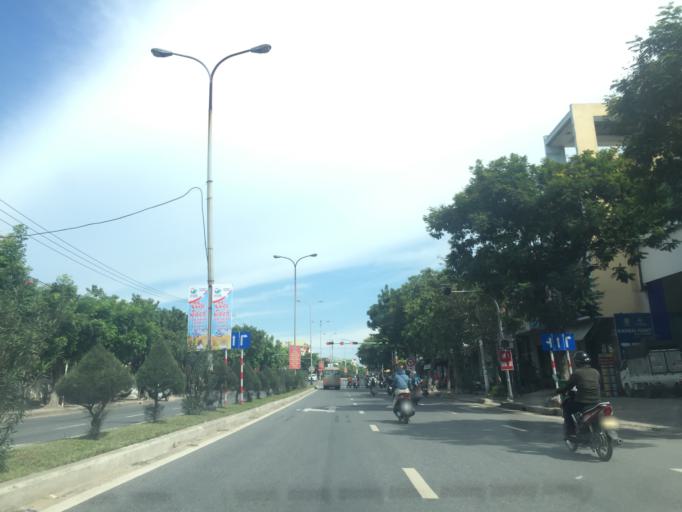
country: VN
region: Da Nang
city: Lien Chieu
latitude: 16.0595
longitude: 108.1638
